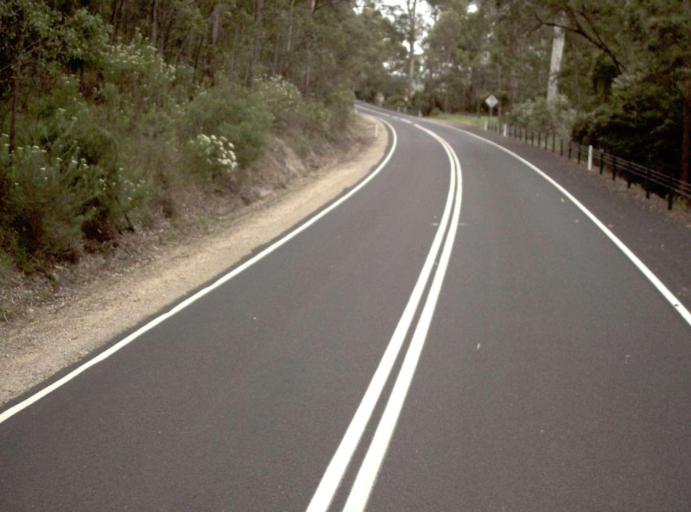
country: AU
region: New South Wales
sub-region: Bombala
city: Bombala
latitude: -37.4692
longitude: 149.1784
